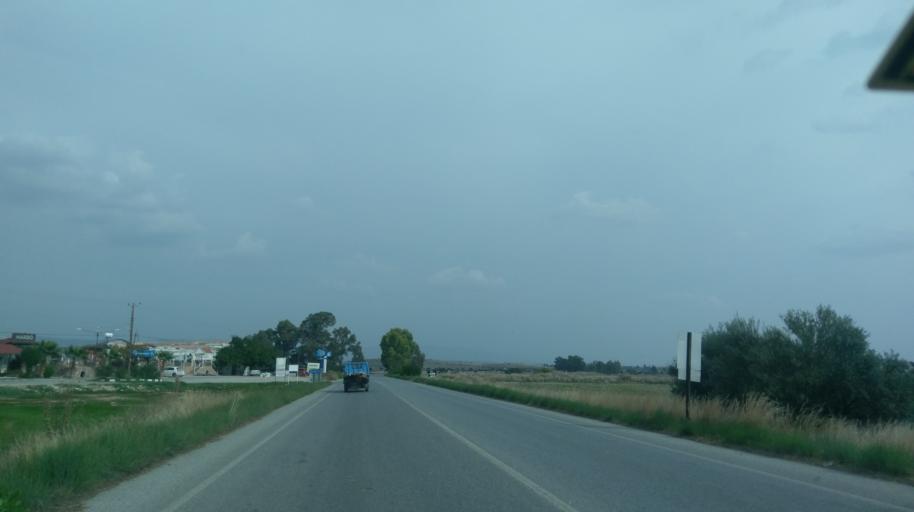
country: CY
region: Ammochostos
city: Lefkonoiko
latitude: 35.2468
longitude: 33.6107
